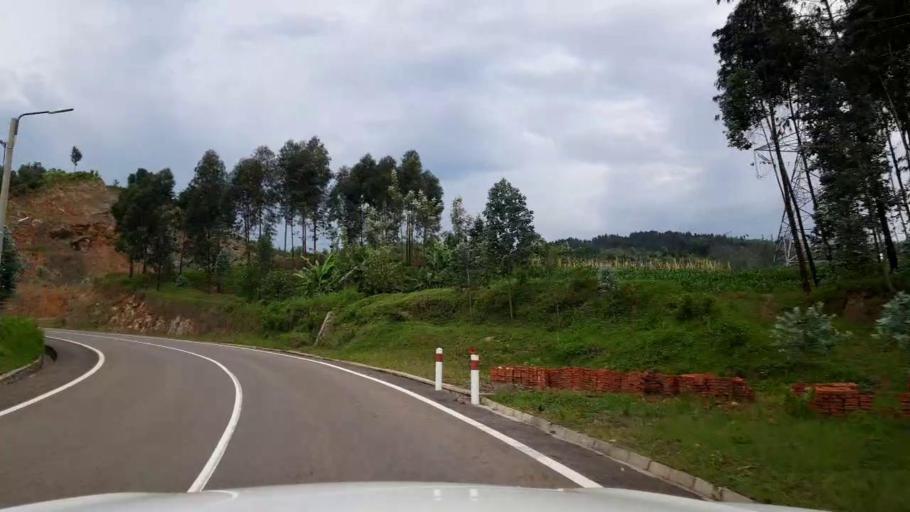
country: RW
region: Western Province
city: Kibuye
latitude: -2.0312
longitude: 29.3970
